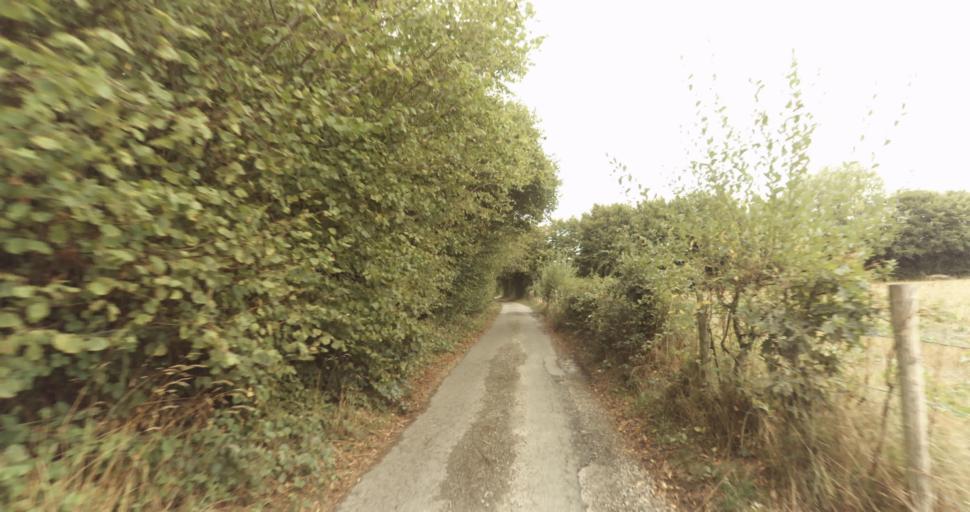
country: FR
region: Lower Normandy
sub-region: Departement de l'Orne
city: Gace
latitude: 48.8655
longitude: 0.3154
